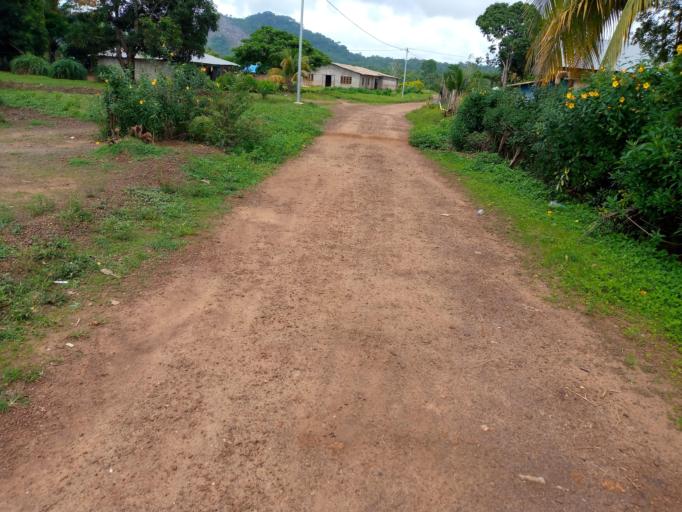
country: SL
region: Southern Province
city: Mogbwemo
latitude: 7.7625
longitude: -12.3118
